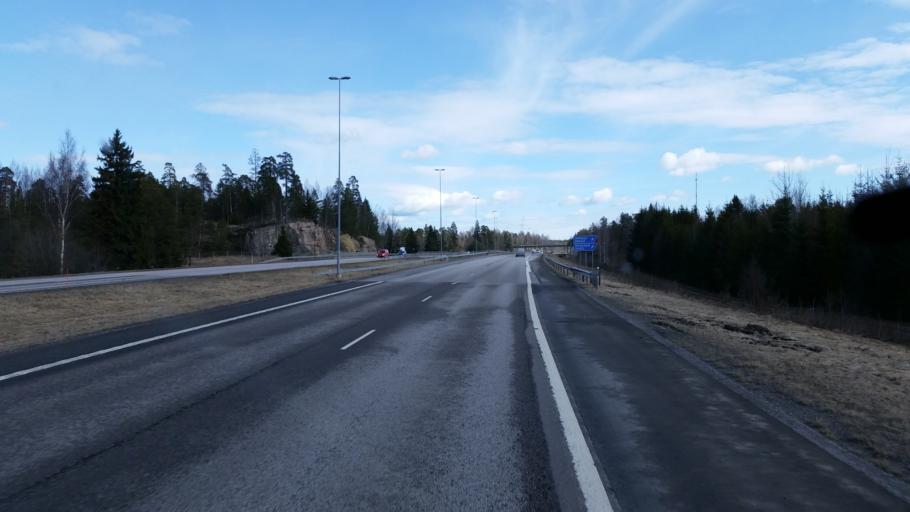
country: FI
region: Uusimaa
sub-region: Porvoo
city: Porvoo
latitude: 60.3676
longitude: 25.5571
